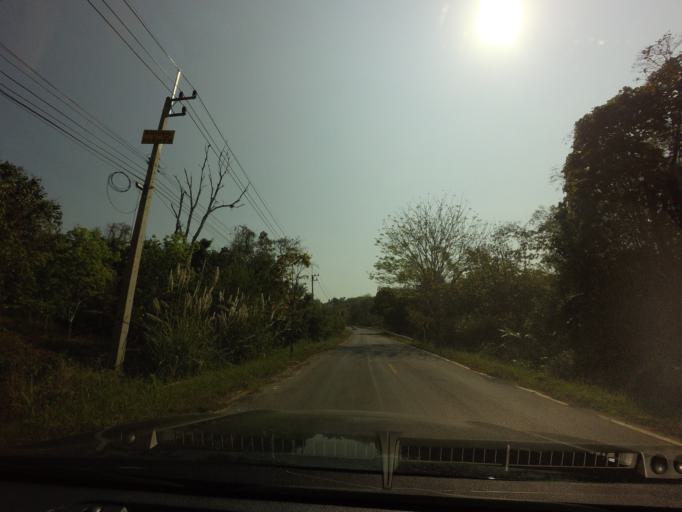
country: TH
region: Kanchanaburi
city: Thong Pha Phum
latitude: 14.6535
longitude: 98.5518
